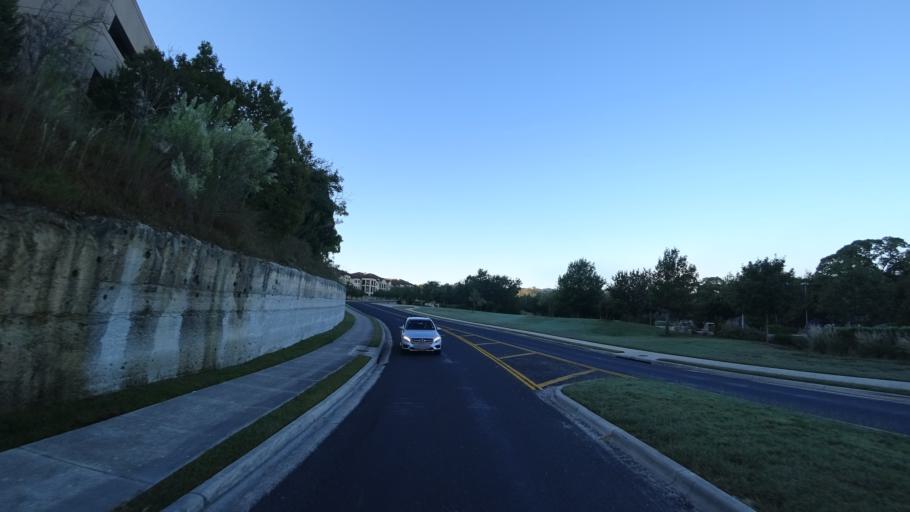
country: US
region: Texas
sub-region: Travis County
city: West Lake Hills
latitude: 30.3354
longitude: -97.8097
